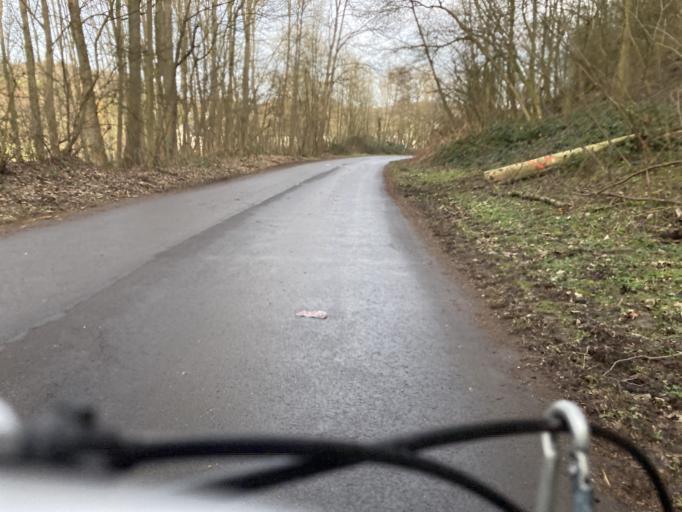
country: DE
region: North Rhine-Westphalia
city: Hattingen
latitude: 51.3830
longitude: 7.1091
